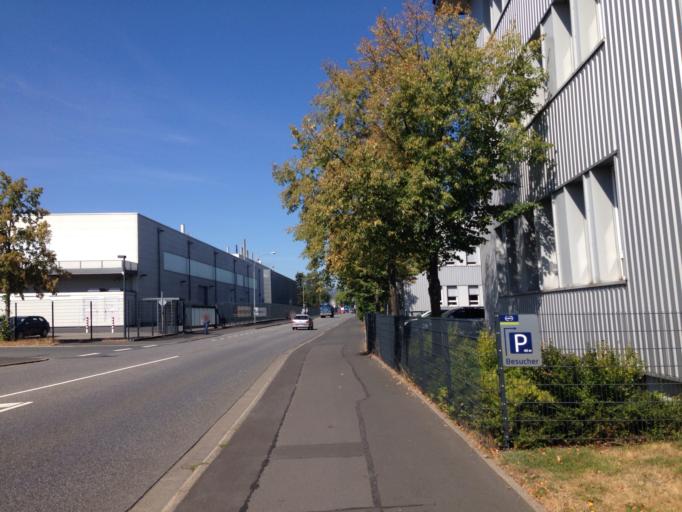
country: DE
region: Hesse
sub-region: Regierungsbezirk Giessen
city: Heuchelheim
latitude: 50.5899
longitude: 8.6338
